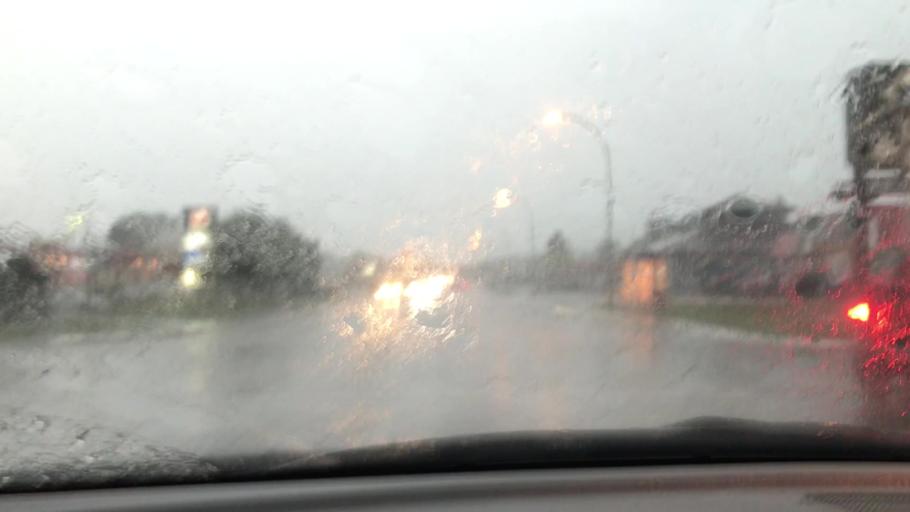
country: CA
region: Alberta
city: Edmonton
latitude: 53.5412
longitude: -113.4368
